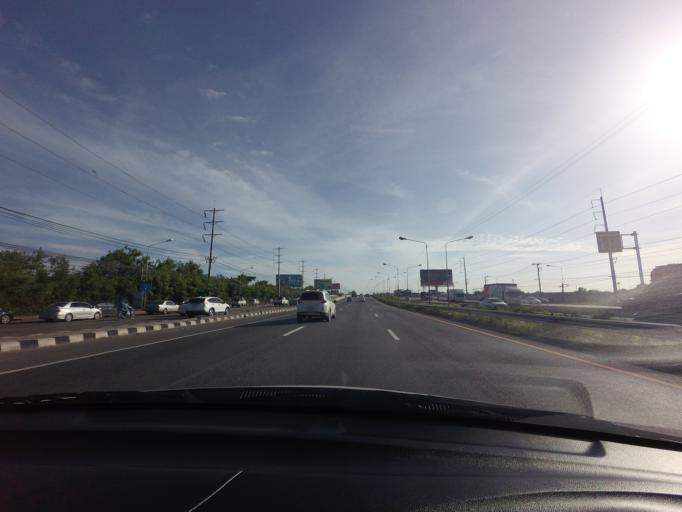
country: TH
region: Nonthaburi
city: Bang Bua Thong
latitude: 13.9155
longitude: 100.4105
